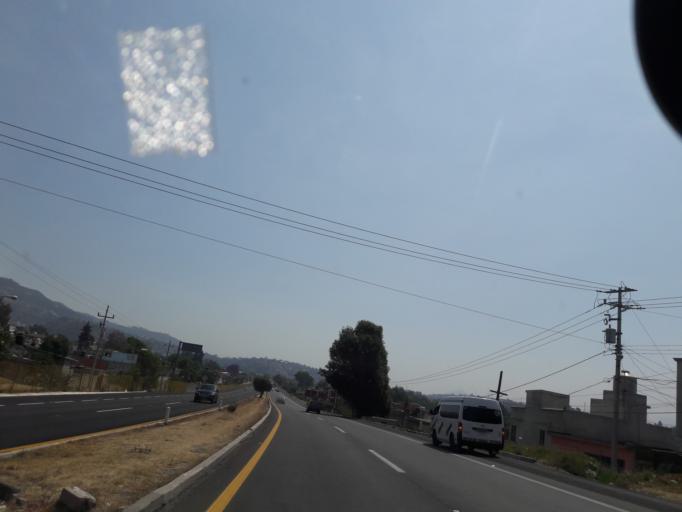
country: MX
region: Tlaxcala
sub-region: Totolac
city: Zaragoza
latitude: 19.3207
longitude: -98.2616
